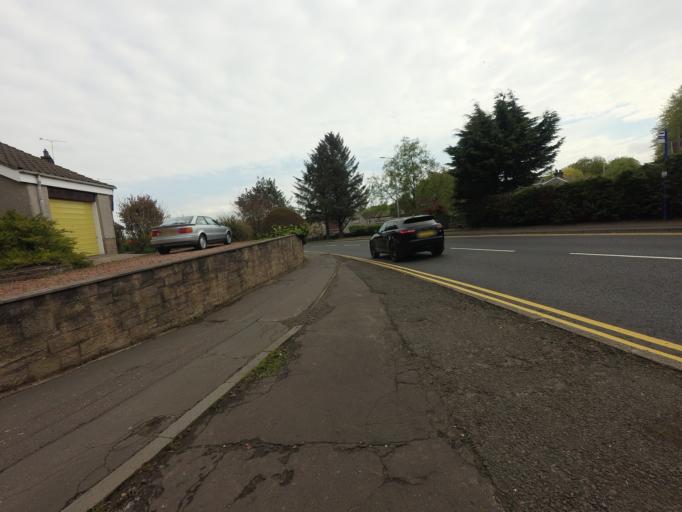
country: GB
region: Scotland
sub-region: Falkirk
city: Polmont
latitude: 55.9854
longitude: -3.7140
